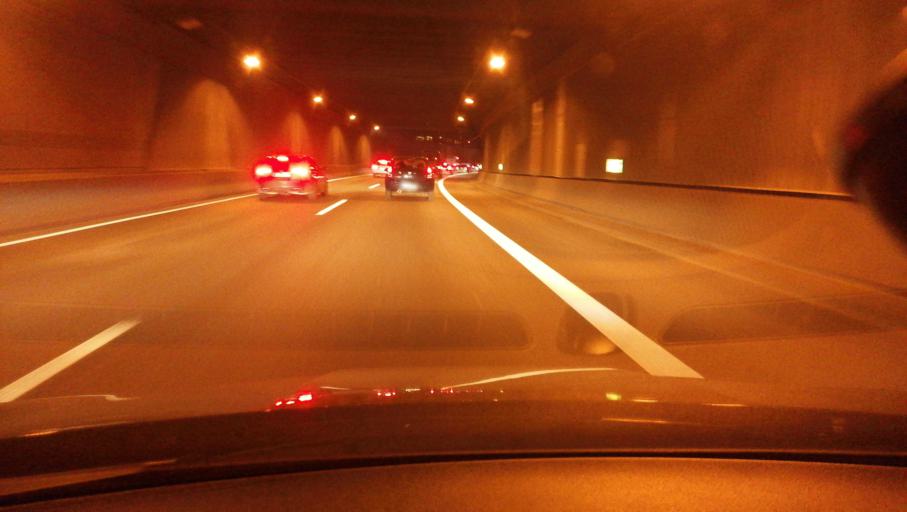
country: DE
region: North Rhine-Westphalia
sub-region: Regierungsbezirk Arnsberg
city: Bochum
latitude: 51.4955
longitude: 7.2386
